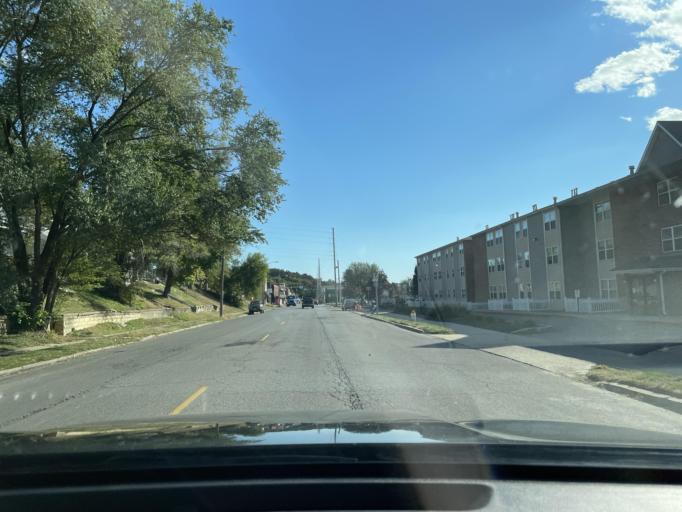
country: US
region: Kansas
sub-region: Doniphan County
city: Elwood
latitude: 39.7137
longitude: -94.8623
